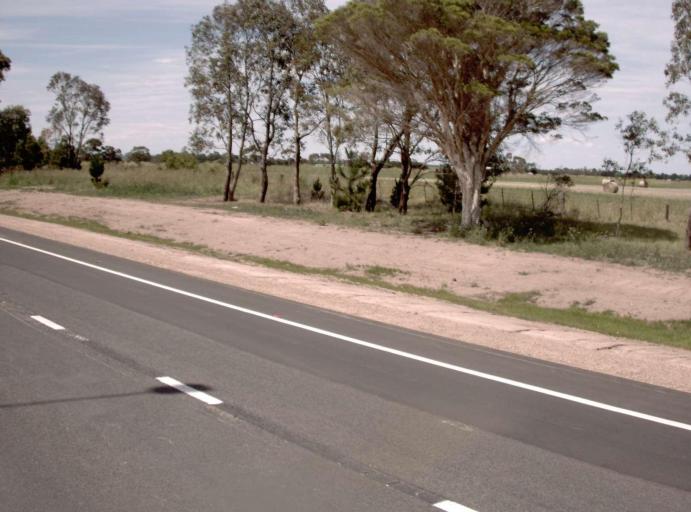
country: AU
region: Victoria
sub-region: Wellington
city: Sale
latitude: -38.0792
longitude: 147.0717
